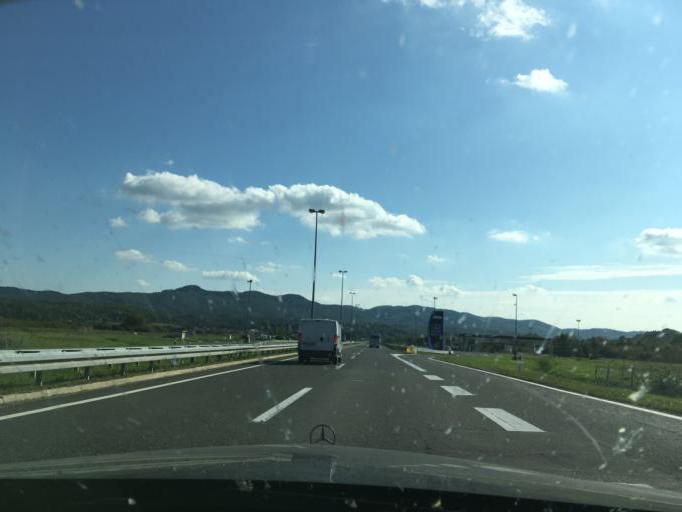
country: HR
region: Varazdinska
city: Ljubescica
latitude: 46.1726
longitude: 16.3748
